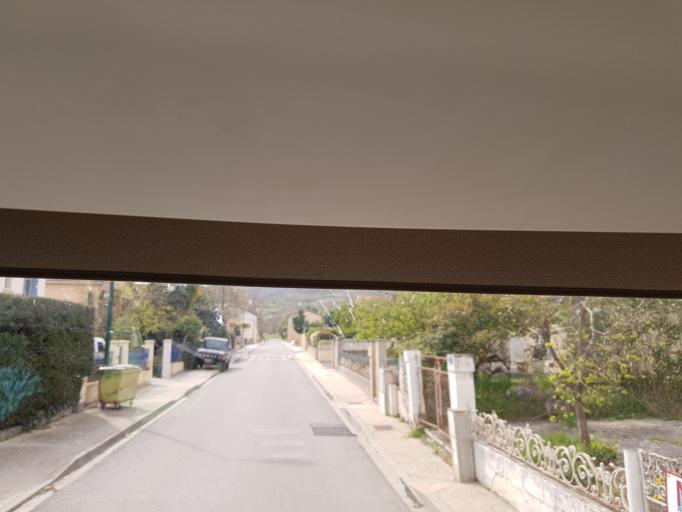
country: FR
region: Languedoc-Roussillon
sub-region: Departement de l'Aude
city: Esperaza
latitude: 42.9155
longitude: 2.2052
